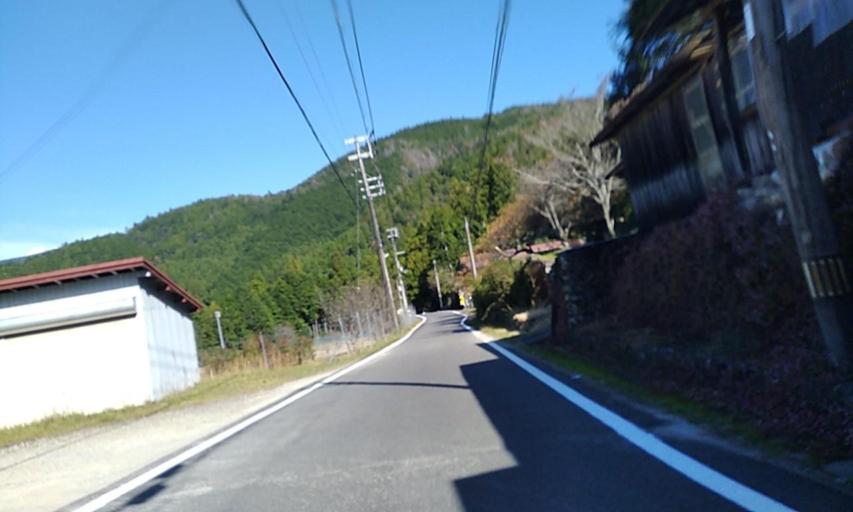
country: JP
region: Wakayama
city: Shingu
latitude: 33.9296
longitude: 135.9794
